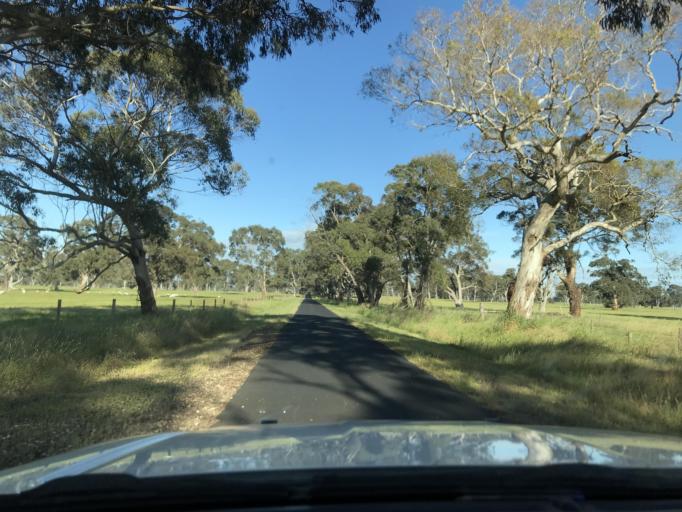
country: AU
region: South Australia
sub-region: Wattle Range
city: Penola
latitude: -37.2021
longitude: 140.9951
